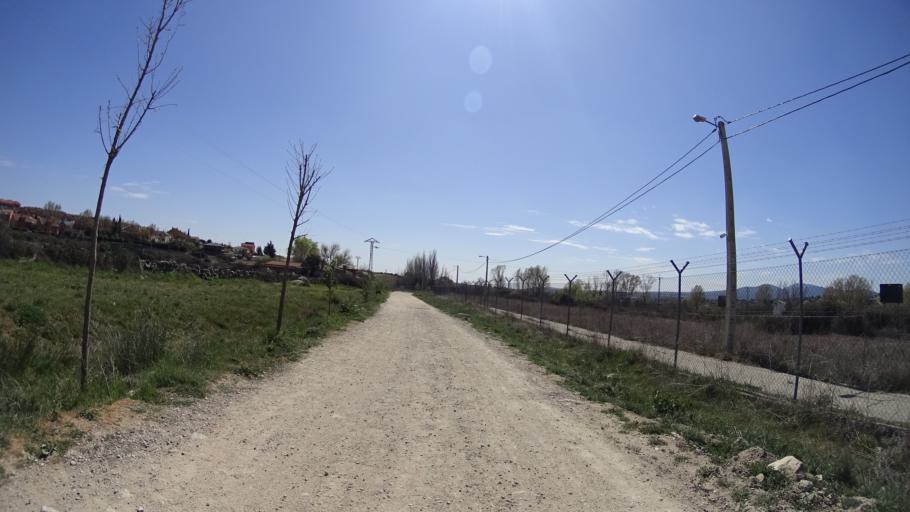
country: ES
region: Madrid
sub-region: Provincia de Madrid
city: Colmenar Viejo
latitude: 40.6735
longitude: -3.7856
